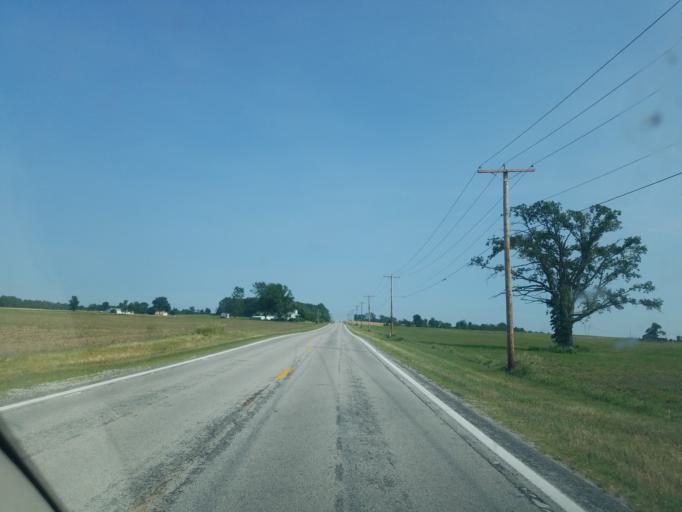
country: US
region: Ohio
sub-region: Wyandot County
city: Carey
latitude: 41.0185
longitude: -83.2891
